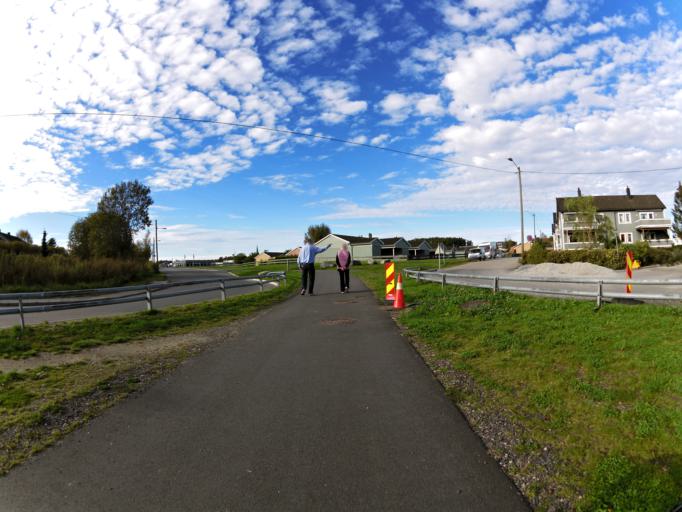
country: NO
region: Ostfold
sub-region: Sarpsborg
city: Sarpsborg
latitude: 59.2866
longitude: 11.0935
